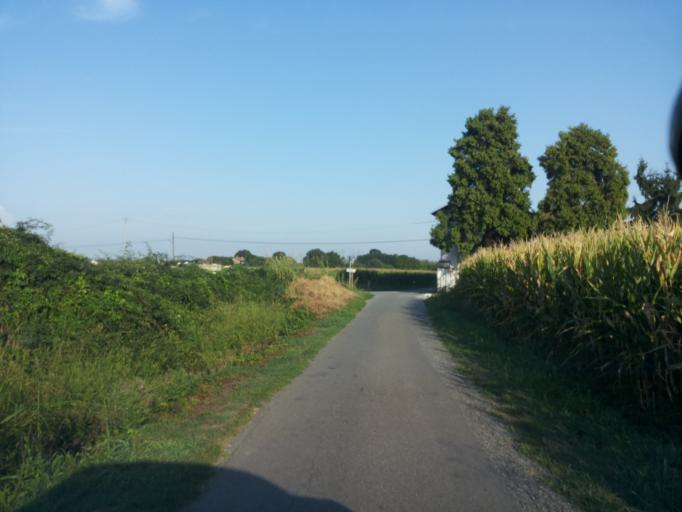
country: IT
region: Piedmont
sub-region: Provincia di Biella
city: Cavaglia
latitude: 45.4015
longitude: 8.0989
